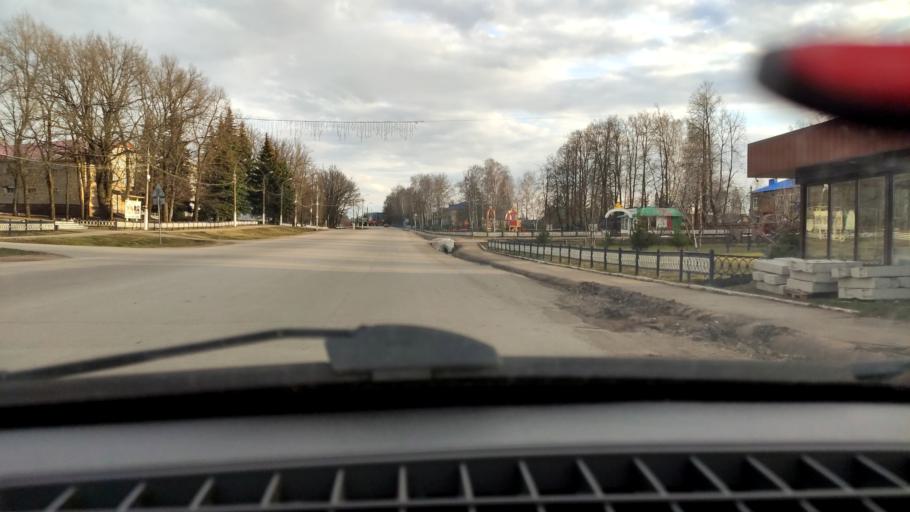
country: RU
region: Bashkortostan
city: Tolbazy
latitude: 54.0146
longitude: 55.8863
